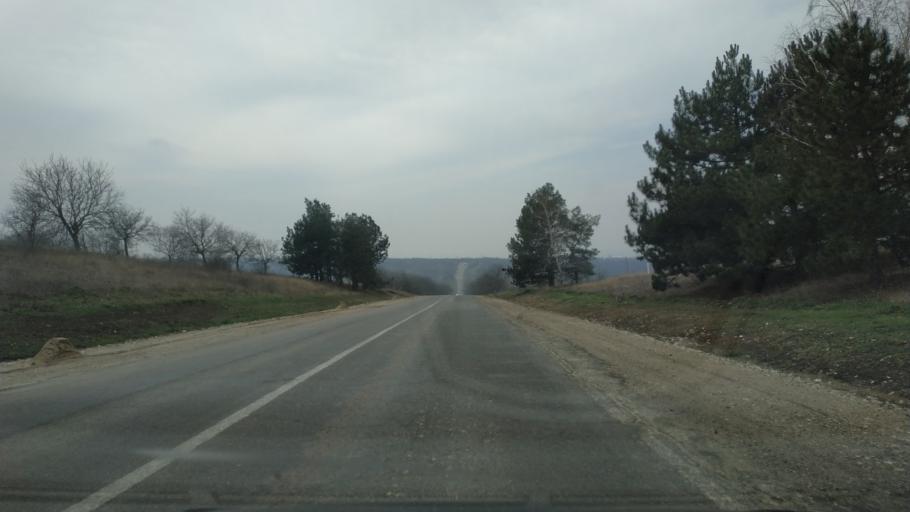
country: MD
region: Cahul
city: Cahul
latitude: 45.9306
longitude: 28.2716
